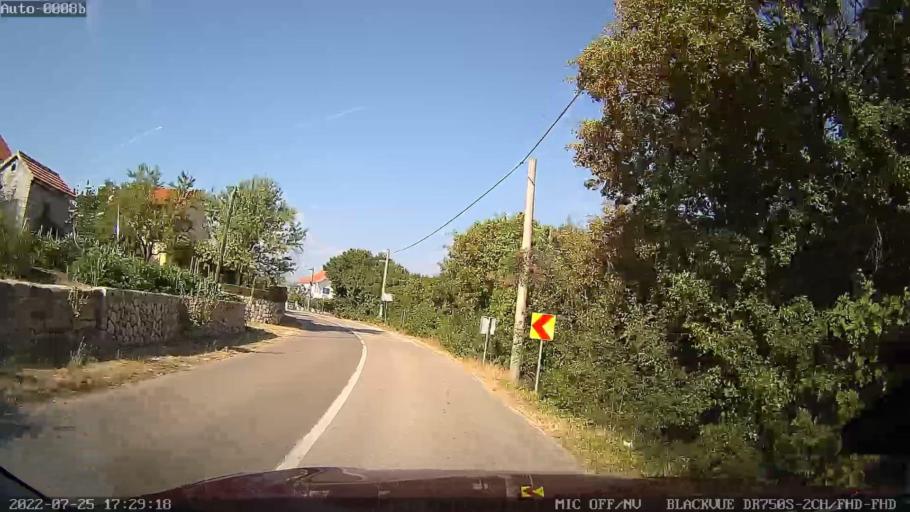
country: HR
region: Zadarska
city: Pridraga
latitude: 44.1595
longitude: 15.5126
